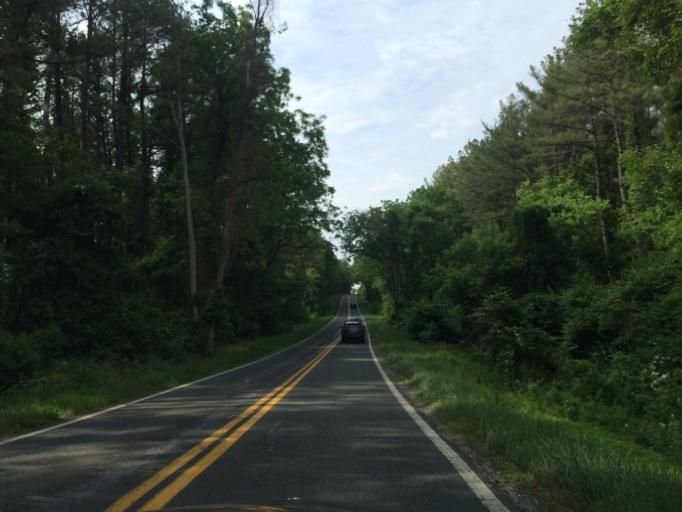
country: US
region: Maryland
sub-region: Baltimore County
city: Reisterstown
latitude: 39.4534
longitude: -76.8971
